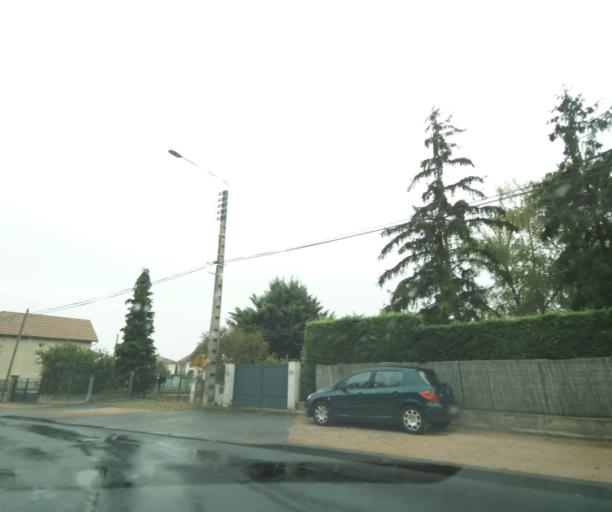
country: FR
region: Auvergne
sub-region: Departement du Puy-de-Dome
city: Cebazat
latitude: 45.8256
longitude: 3.1045
